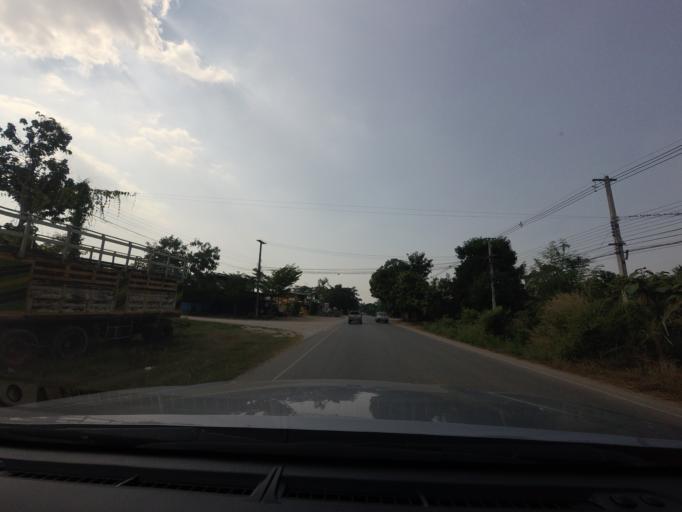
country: TH
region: Phitsanulok
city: Bang Rakam
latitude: 16.7481
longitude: 100.0844
